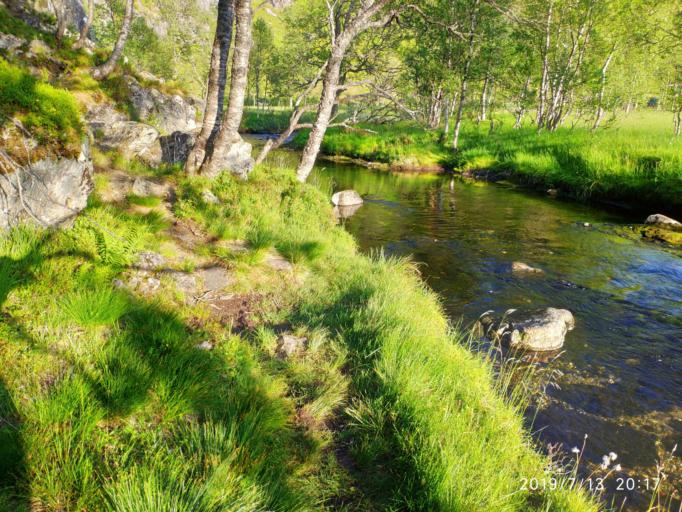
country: NO
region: Rogaland
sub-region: Sauda
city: Sauda
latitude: 59.8391
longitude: 6.3483
